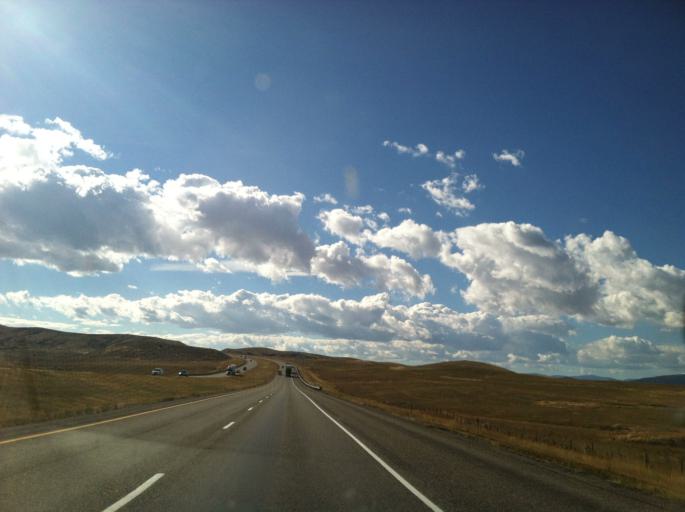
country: US
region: Montana
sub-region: Gallatin County
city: Three Forks
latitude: 45.9201
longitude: -111.6445
